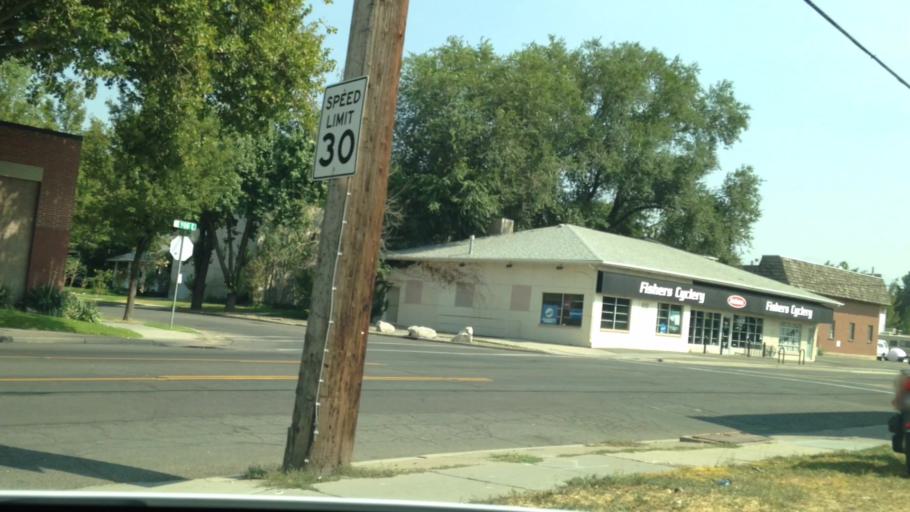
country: US
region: Utah
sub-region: Salt Lake County
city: South Salt Lake
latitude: 40.7241
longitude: -111.8656
